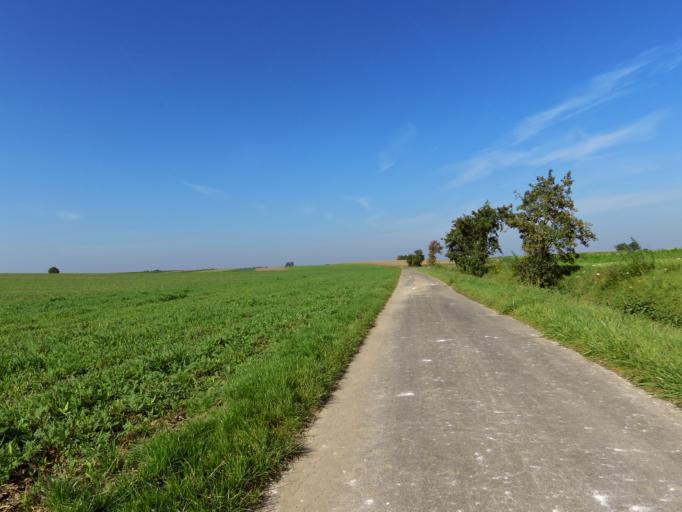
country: DE
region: North Rhine-Westphalia
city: Baesweiler
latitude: 50.9320
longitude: 6.1783
